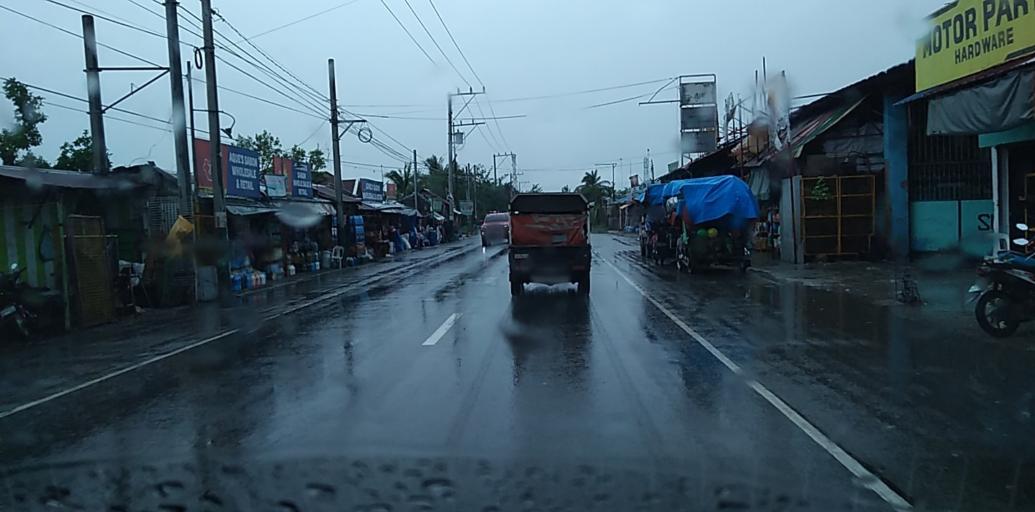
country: PH
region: Central Luzon
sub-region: Province of Bulacan
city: Bulualto
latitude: 15.2125
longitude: 120.9554
